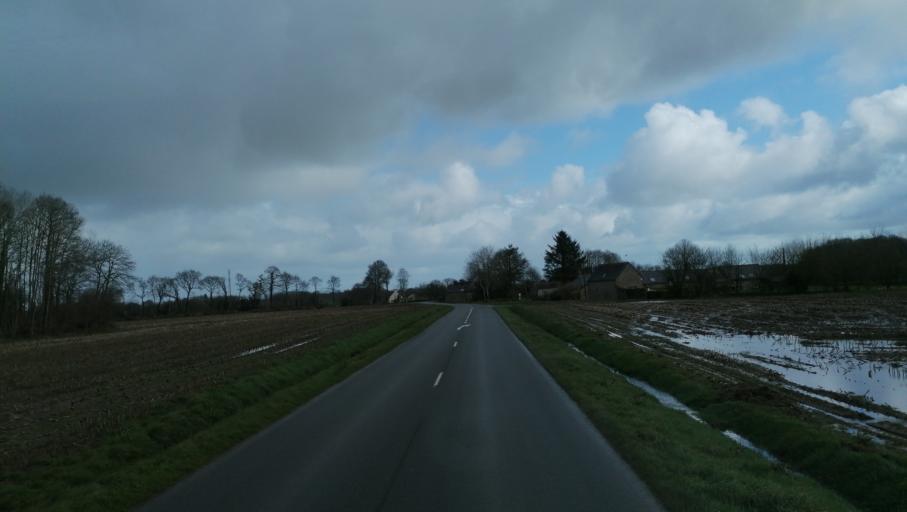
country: FR
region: Brittany
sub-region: Departement des Cotes-d'Armor
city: Lanrodec
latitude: 48.5272
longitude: -3.0176
